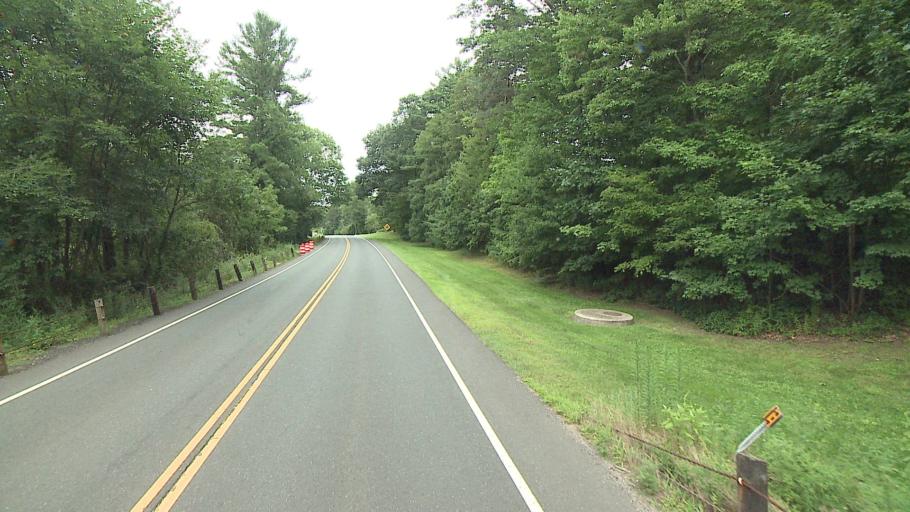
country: US
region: Connecticut
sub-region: New Haven County
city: Middlebury
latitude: 41.5322
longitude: -73.1250
